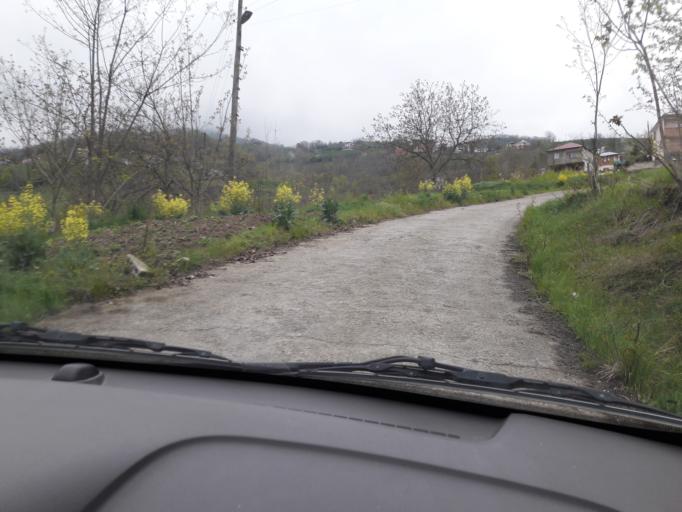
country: TR
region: Trabzon
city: Duzkoy
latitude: 40.9285
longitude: 39.4820
